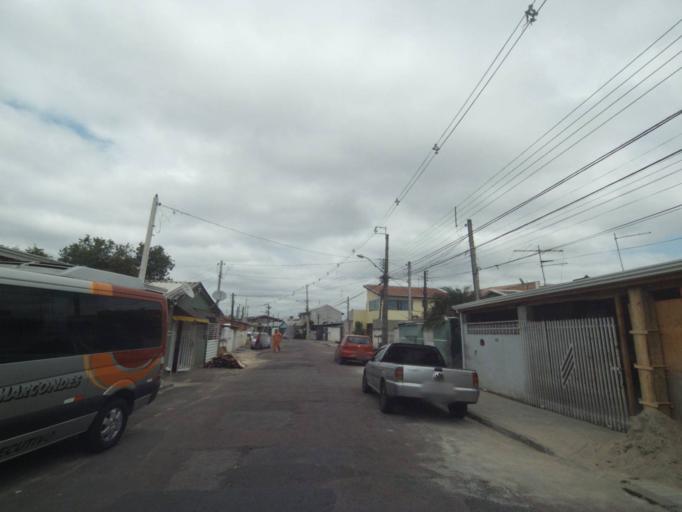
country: BR
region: Parana
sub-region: Sao Jose Dos Pinhais
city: Sao Jose dos Pinhais
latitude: -25.5365
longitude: -49.2655
